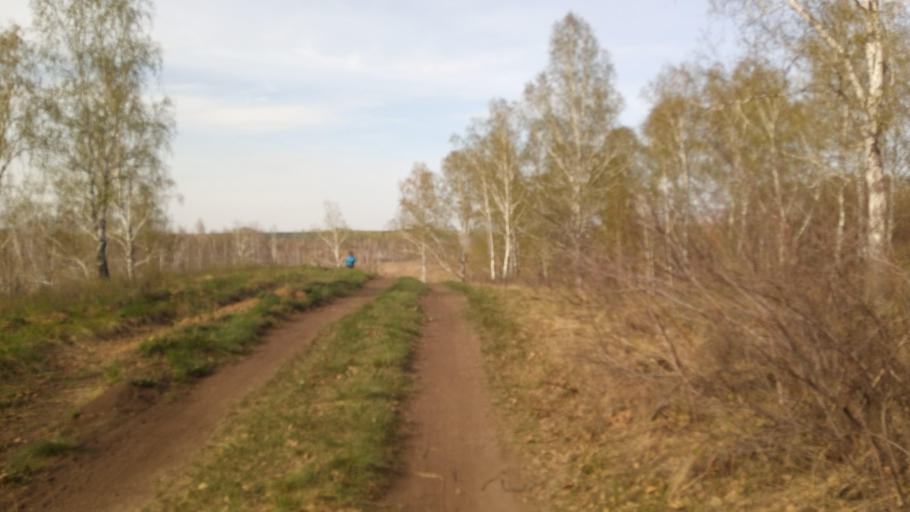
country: RU
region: Chelyabinsk
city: Poletayevo
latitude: 55.0310
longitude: 61.0741
